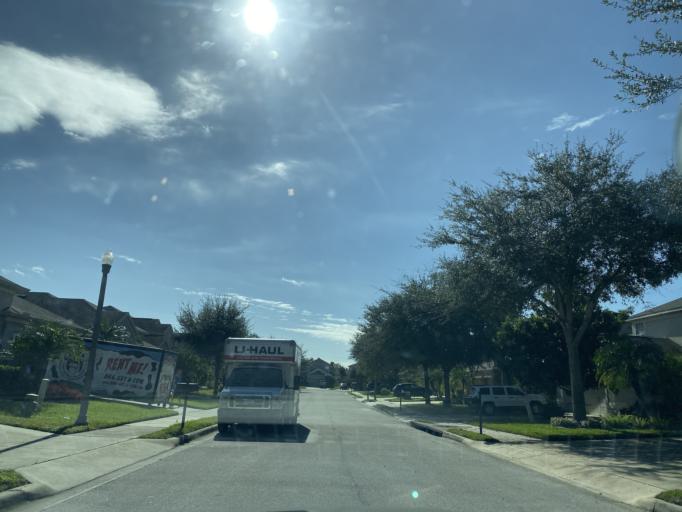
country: US
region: Florida
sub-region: Seminole County
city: Goldenrod
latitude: 28.6145
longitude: -81.2636
